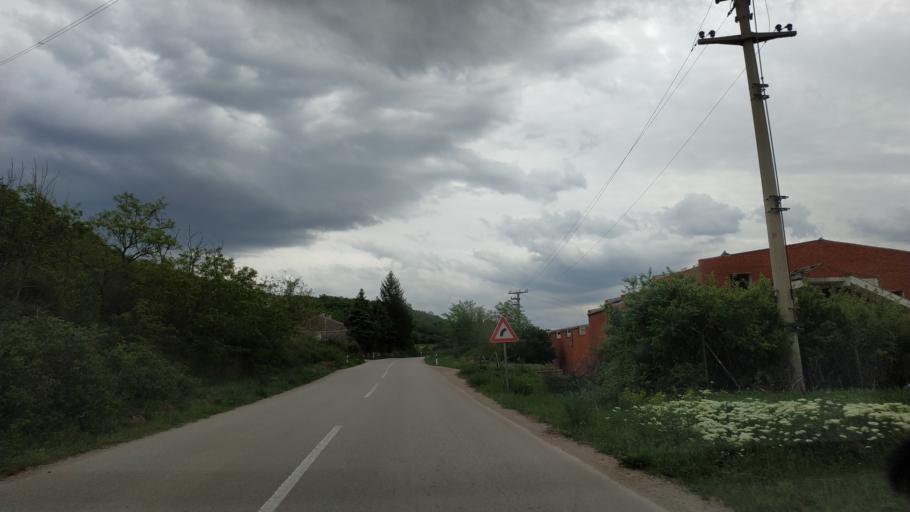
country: RS
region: Central Serbia
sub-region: Nisavski Okrug
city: Aleksinac
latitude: 43.6224
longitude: 21.6923
